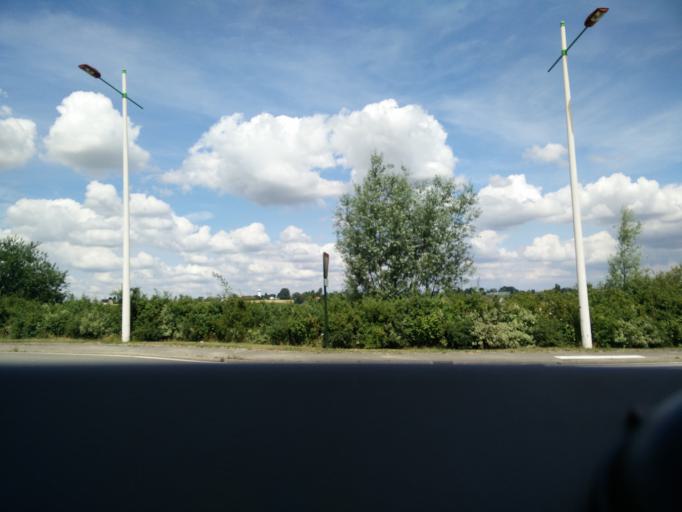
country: FR
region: Nord-Pas-de-Calais
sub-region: Departement du Pas-de-Calais
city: Bethune
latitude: 50.5502
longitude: 2.6297
